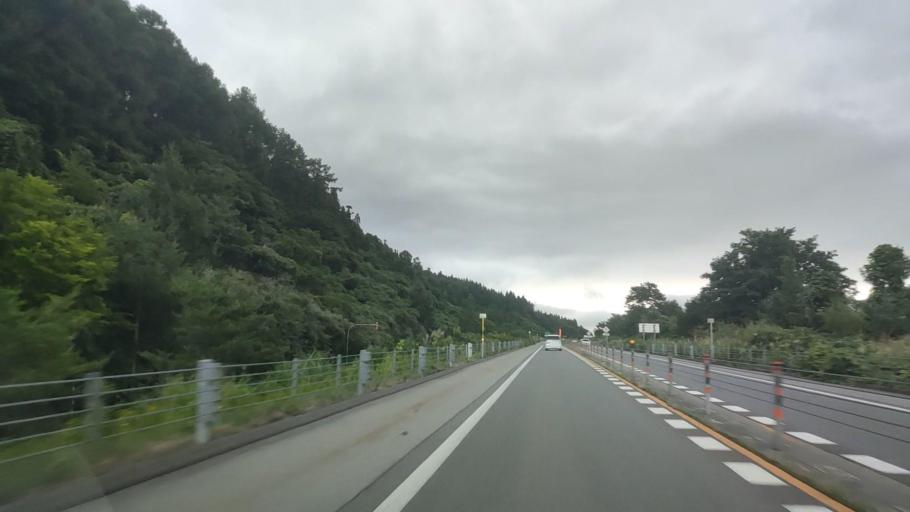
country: JP
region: Hokkaido
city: Nanae
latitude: 41.9108
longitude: 140.6934
